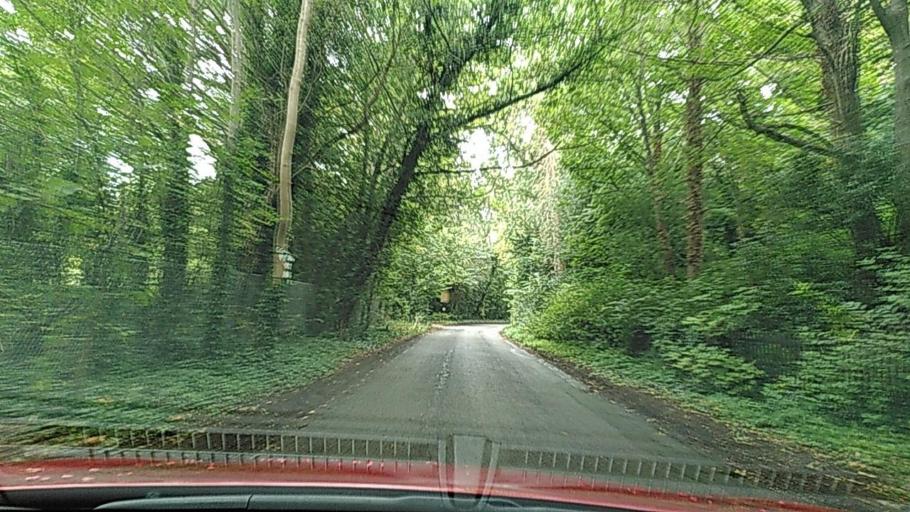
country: GB
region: England
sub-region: Oxfordshire
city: Henley on Thames
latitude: 51.5238
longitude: -0.9212
